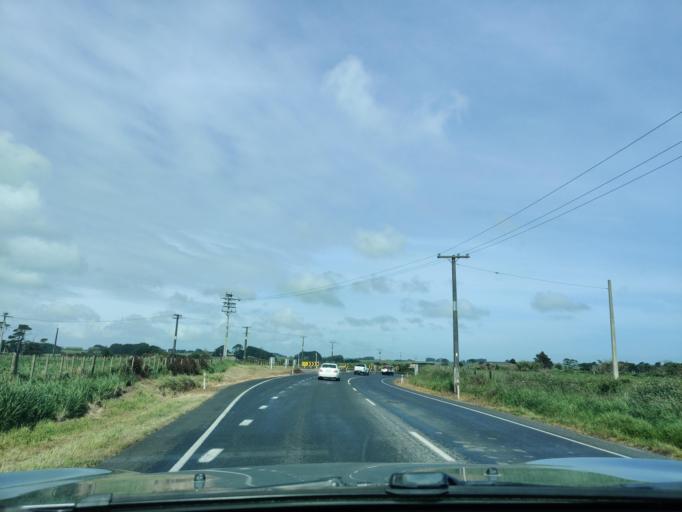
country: NZ
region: Taranaki
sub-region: South Taranaki District
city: Hawera
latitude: -39.6305
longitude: 174.3761
